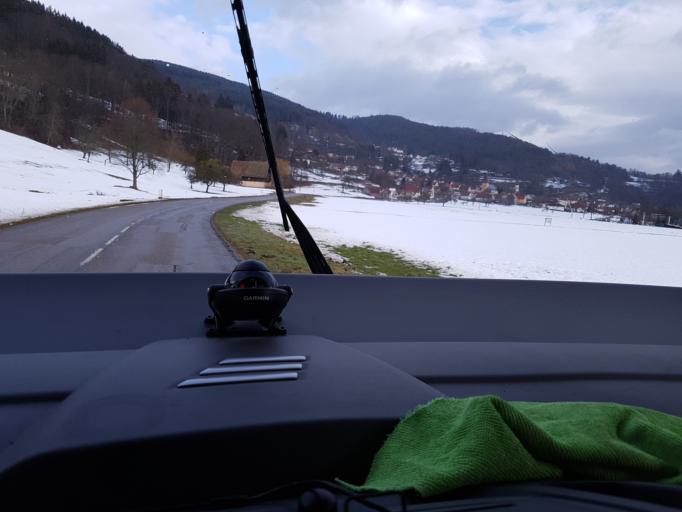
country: FR
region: Alsace
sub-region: Departement du Haut-Rhin
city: Metzeral
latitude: 48.0192
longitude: 7.0749
